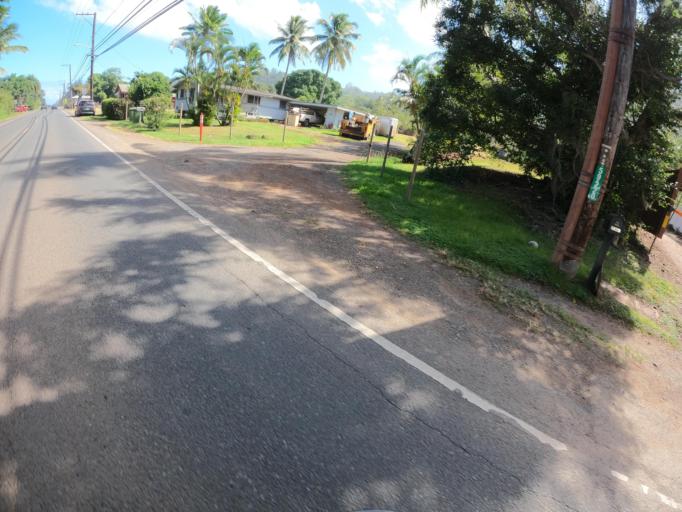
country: US
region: Hawaii
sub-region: Honolulu County
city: Pupukea
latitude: 21.6703
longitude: -158.0445
